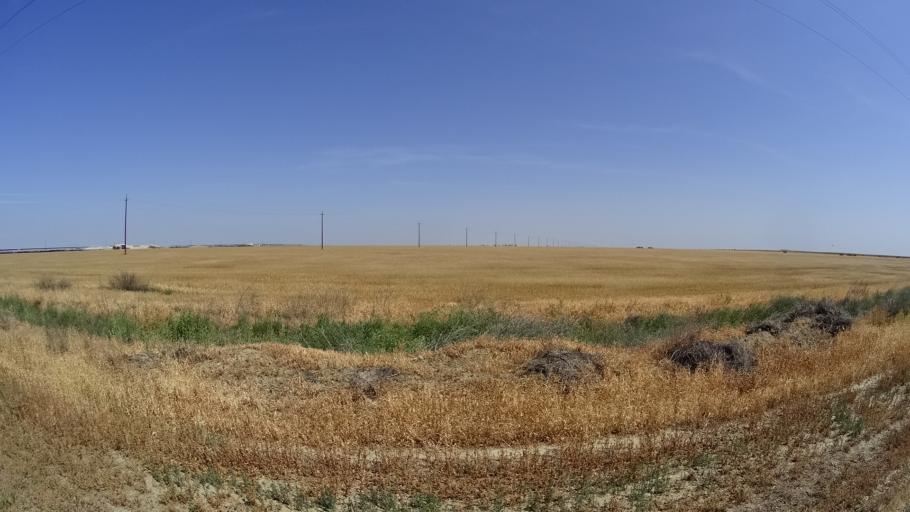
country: US
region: California
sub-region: Kings County
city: Kettleman City
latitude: 36.0941
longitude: -119.9278
